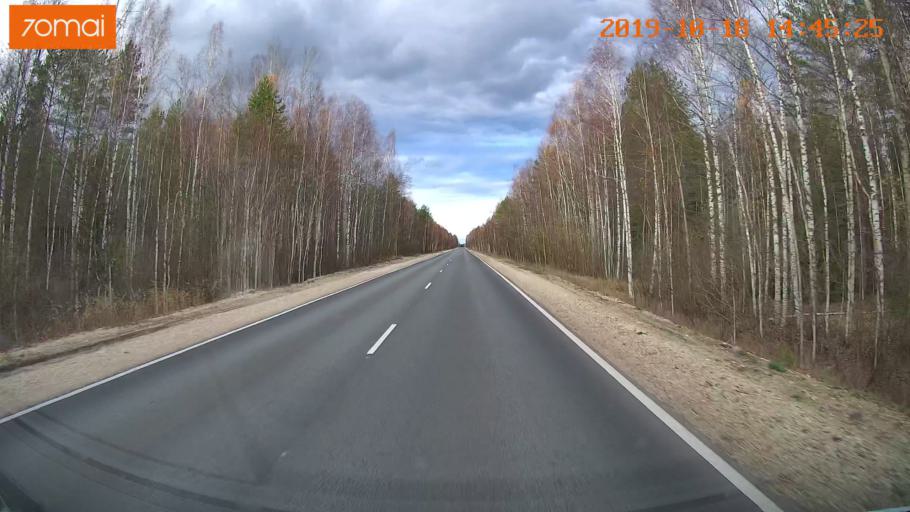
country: RU
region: Vladimir
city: Velikodvorskiy
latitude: 55.3547
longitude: 40.6789
